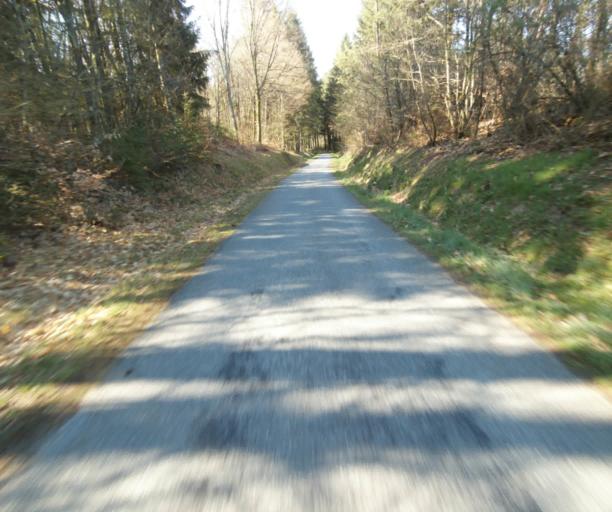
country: FR
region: Limousin
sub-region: Departement de la Correze
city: Correze
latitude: 45.2921
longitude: 1.9193
